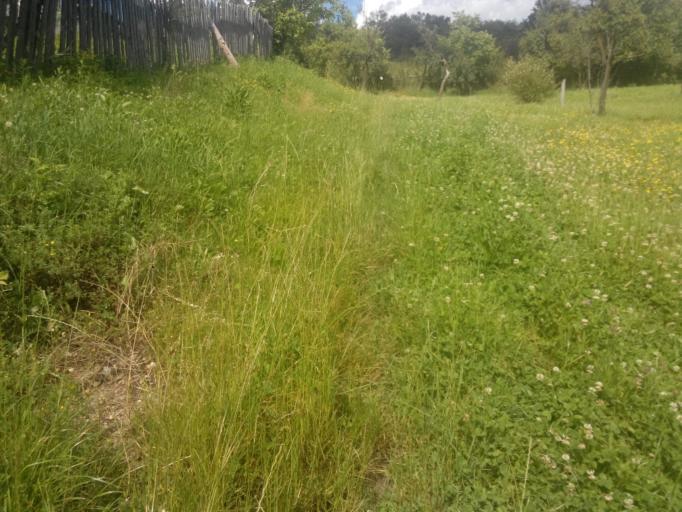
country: RO
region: Arges
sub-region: Comuna Baiculesti
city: Tutana
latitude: 45.0410
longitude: 24.6530
